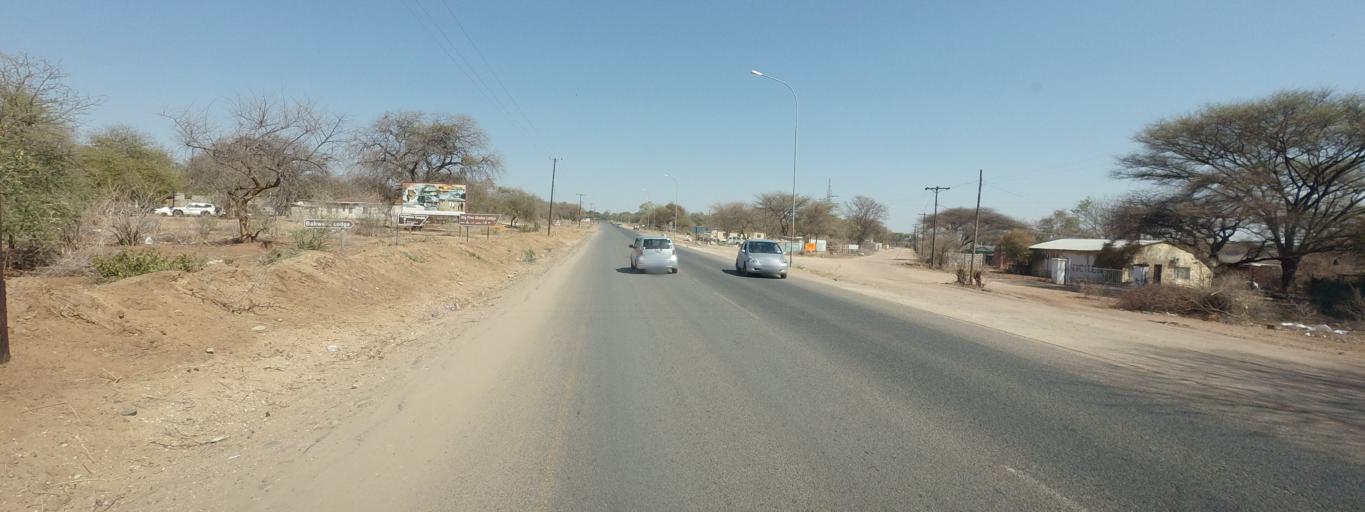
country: BW
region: North West
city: Kasane
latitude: -17.8015
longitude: 25.2400
